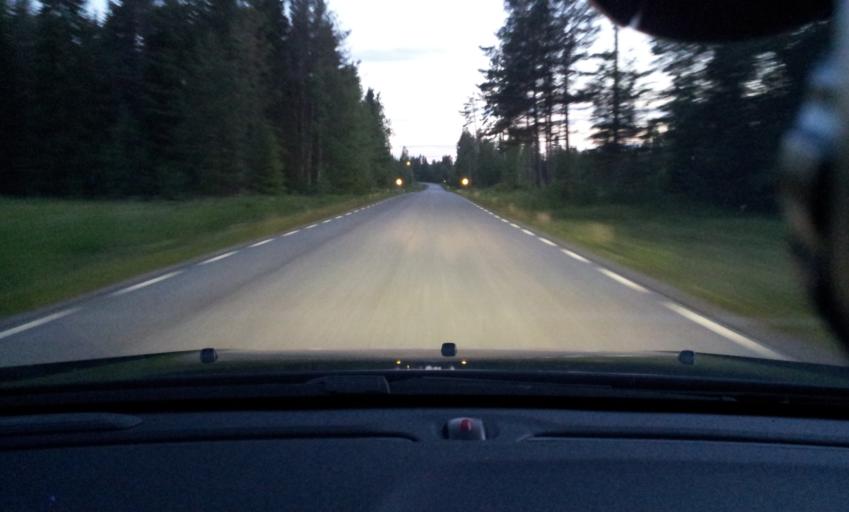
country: SE
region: Jaemtland
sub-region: Braecke Kommun
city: Braecke
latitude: 62.7637
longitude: 15.3096
